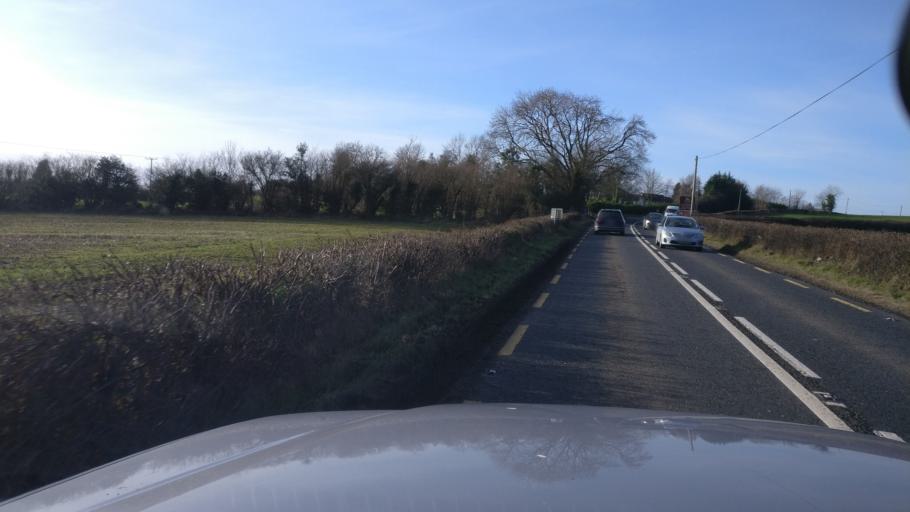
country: IE
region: Leinster
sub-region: Uibh Fhaili
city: Tullamore
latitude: 53.1989
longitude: -7.4272
